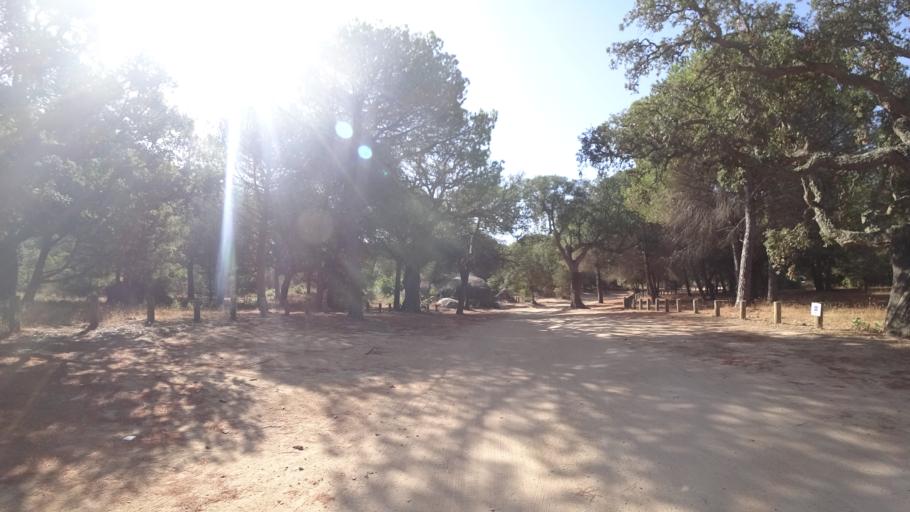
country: FR
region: Corsica
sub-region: Departement de la Corse-du-Sud
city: Porto-Vecchio
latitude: 41.5620
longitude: 9.3371
